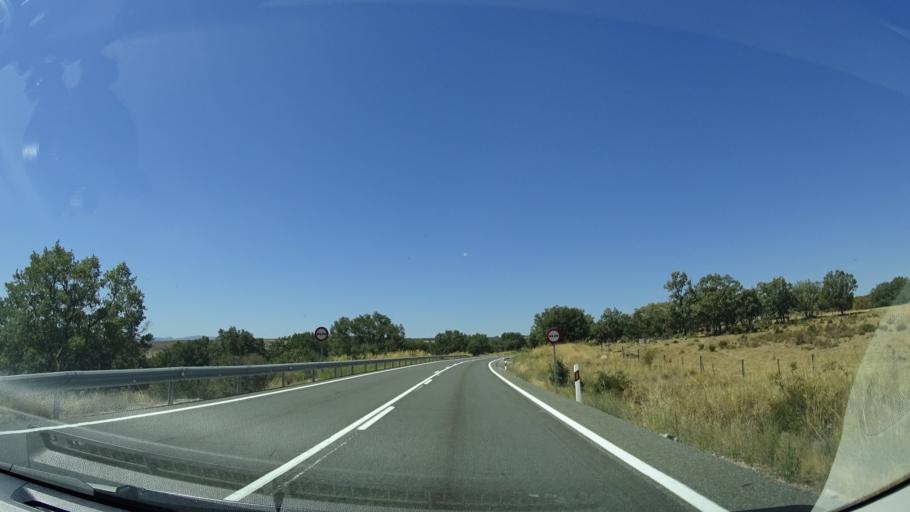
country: ES
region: Castille and Leon
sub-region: Provincia de Avila
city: Navalperal de Pinares
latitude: 40.5930
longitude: -4.4599
